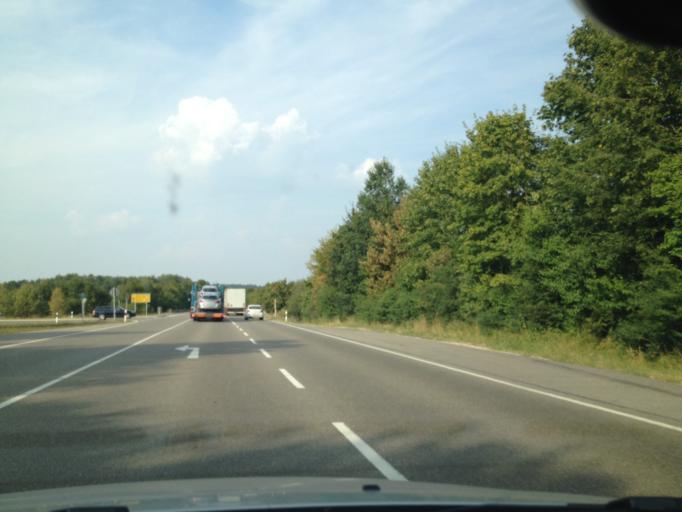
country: DE
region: Bavaria
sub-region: Swabia
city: Monheim
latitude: 48.8445
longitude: 10.8354
